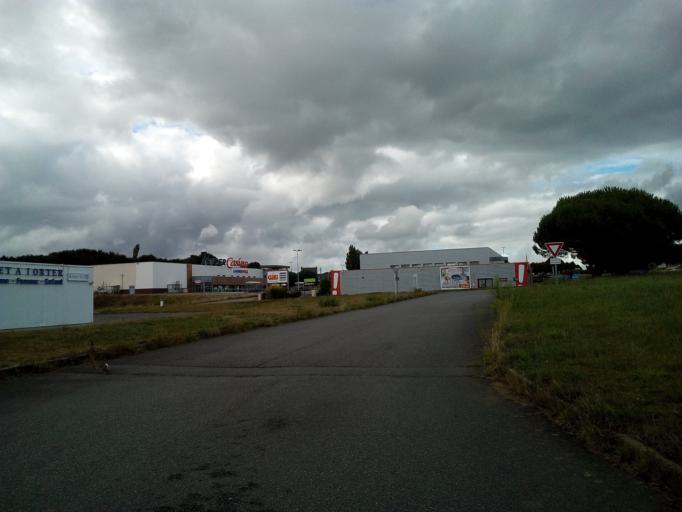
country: FR
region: Brittany
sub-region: Departement du Finistere
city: Landivisiau
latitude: 48.5127
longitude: -4.0533
